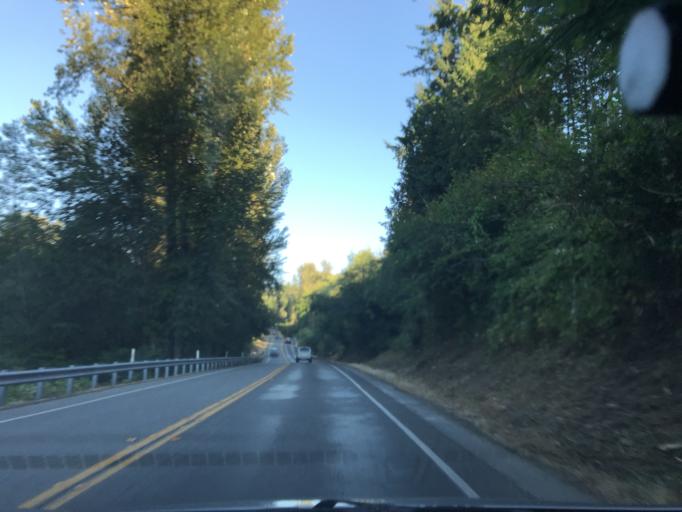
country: US
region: Washington
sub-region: King County
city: Auburn
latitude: 47.2695
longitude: -122.2057
